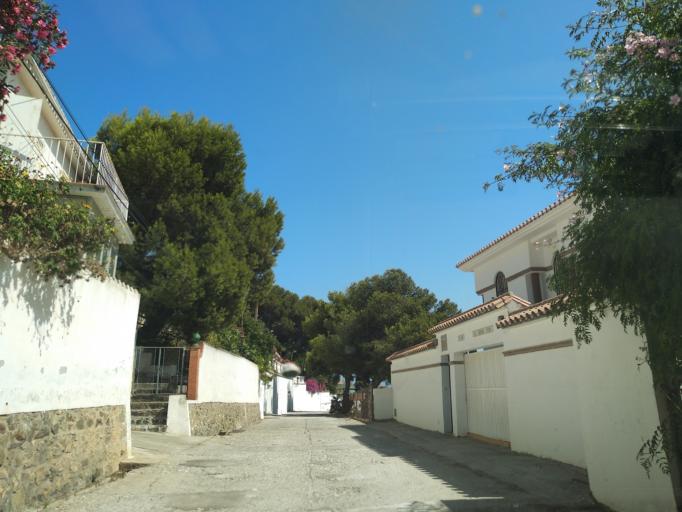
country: ES
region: Andalusia
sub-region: Provincia de Malaga
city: Valdes
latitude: 36.7172
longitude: -4.2019
